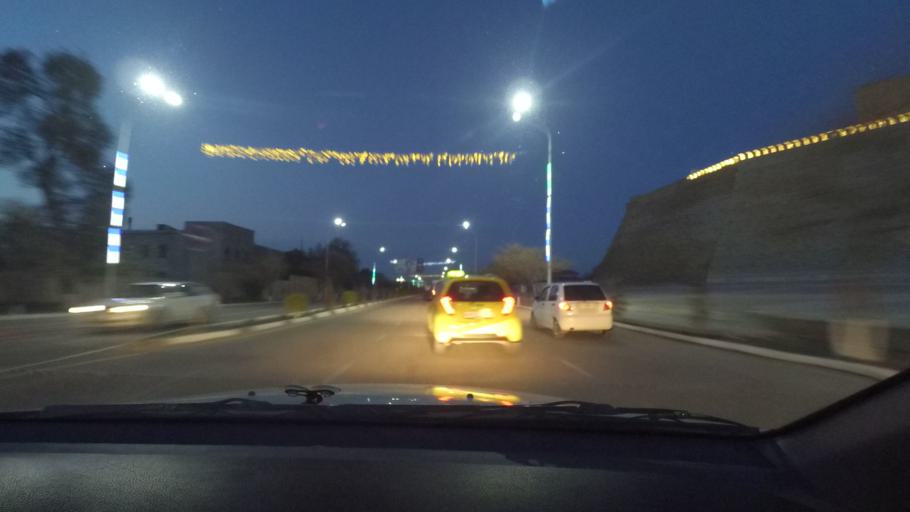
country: UZ
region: Bukhara
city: Bukhara
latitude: 39.7784
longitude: 64.4091
